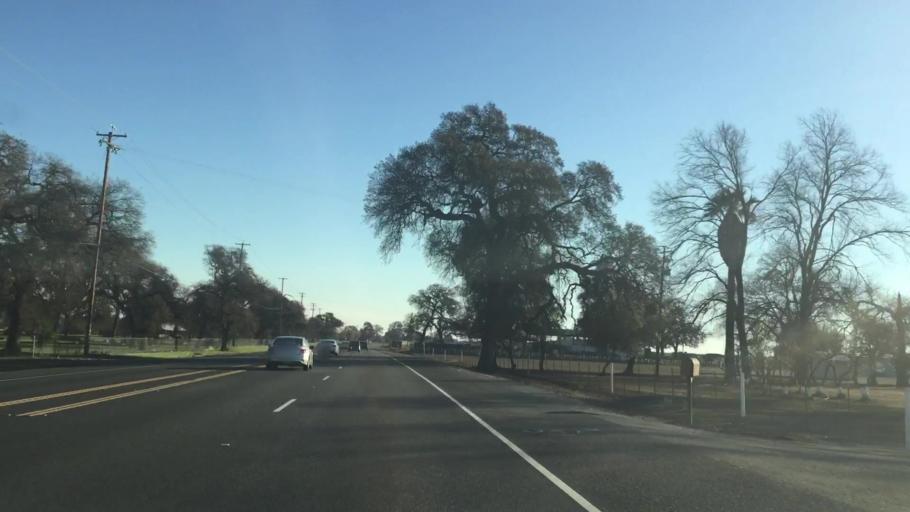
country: US
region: California
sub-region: Butte County
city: Gridley
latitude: 39.3559
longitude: -121.6043
